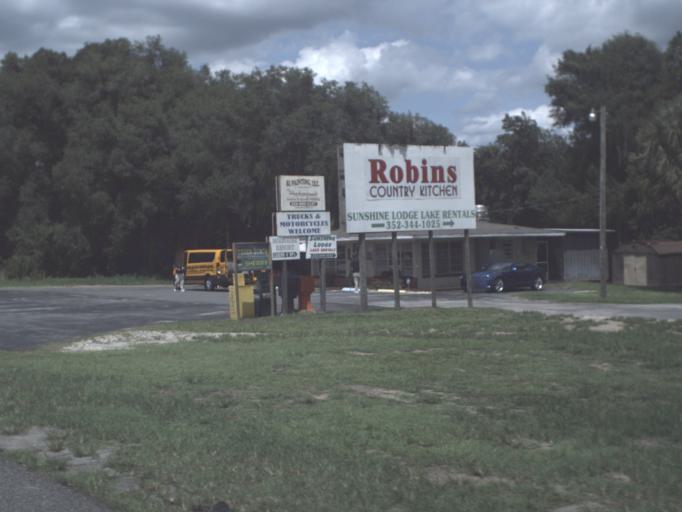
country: US
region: Florida
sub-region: Citrus County
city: Floral City
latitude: 28.7658
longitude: -82.2938
